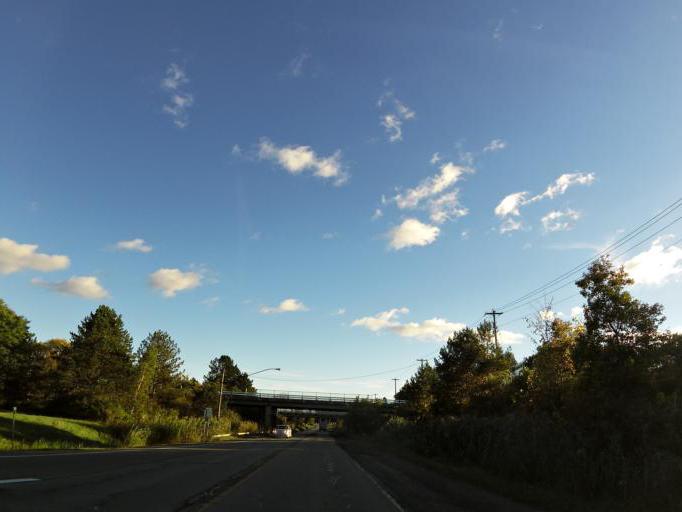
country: US
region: New York
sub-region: Erie County
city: Billington Heights
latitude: 42.7981
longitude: -78.6215
